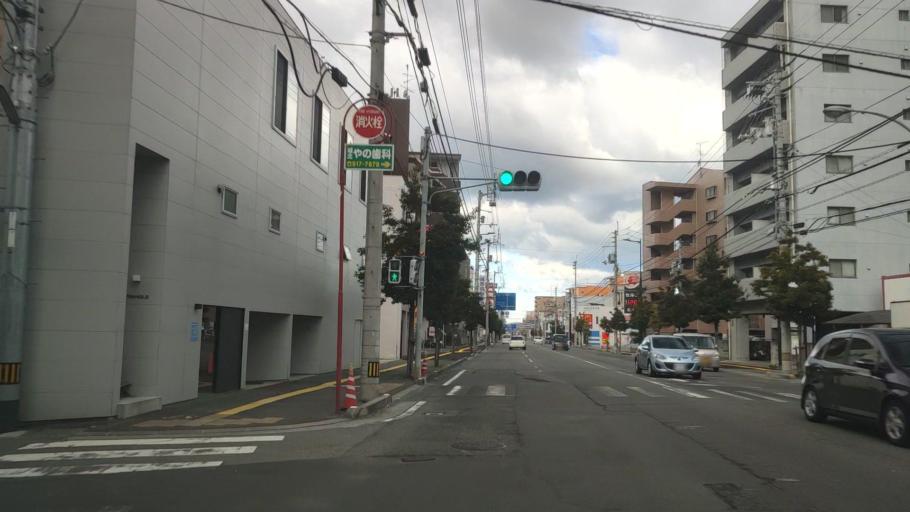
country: JP
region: Ehime
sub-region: Shikoku-chuo Shi
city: Matsuyama
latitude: 33.8533
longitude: 132.7559
